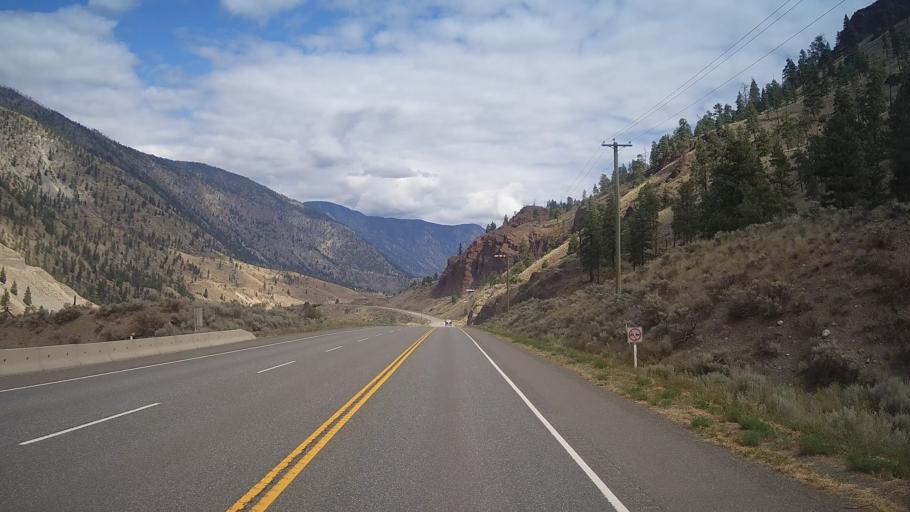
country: CA
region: British Columbia
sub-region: Thompson-Nicola Regional District
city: Ashcroft
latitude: 50.3007
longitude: -121.3924
